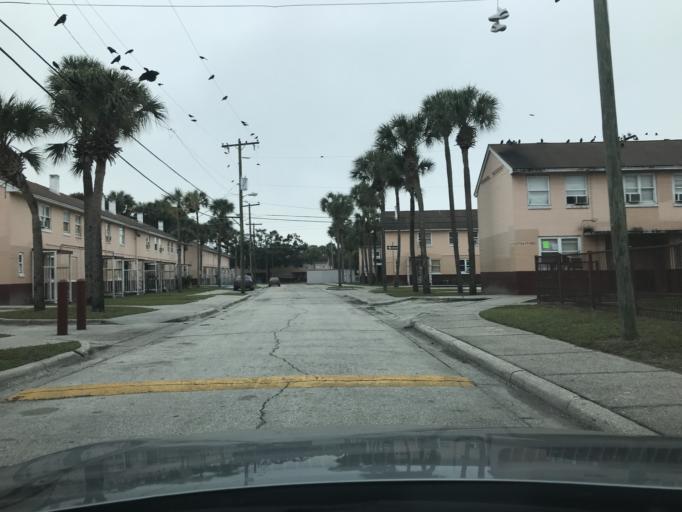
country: US
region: Florida
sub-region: Hillsborough County
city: Tampa
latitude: 27.9791
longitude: -82.4573
